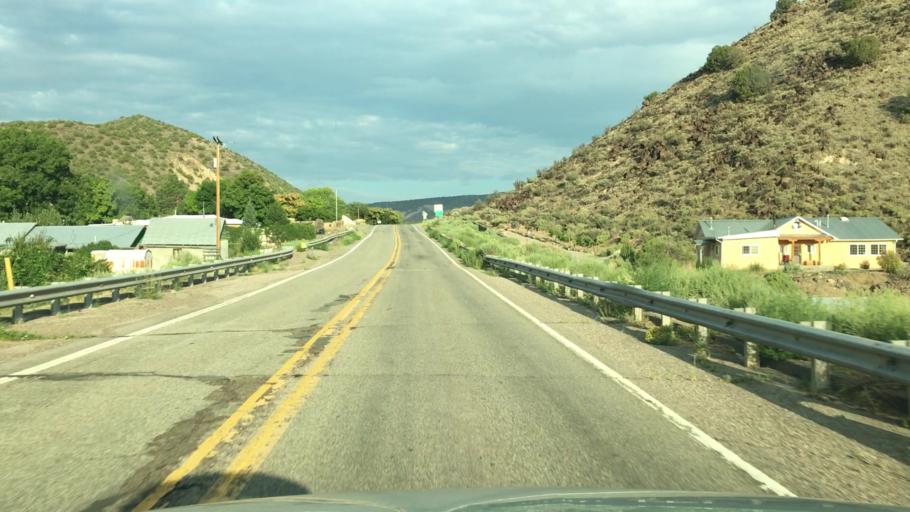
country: US
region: New Mexico
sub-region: Rio Arriba County
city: Chimayo
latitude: 36.2115
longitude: -105.9175
